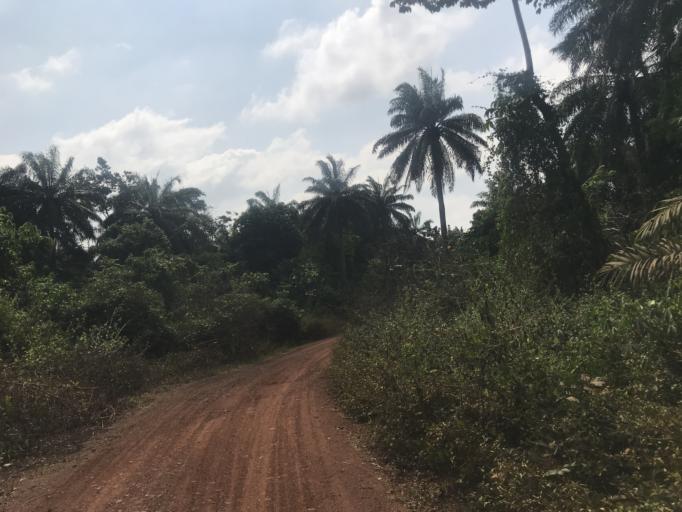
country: NG
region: Osun
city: Ibokun
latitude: 7.8136
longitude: 4.6467
